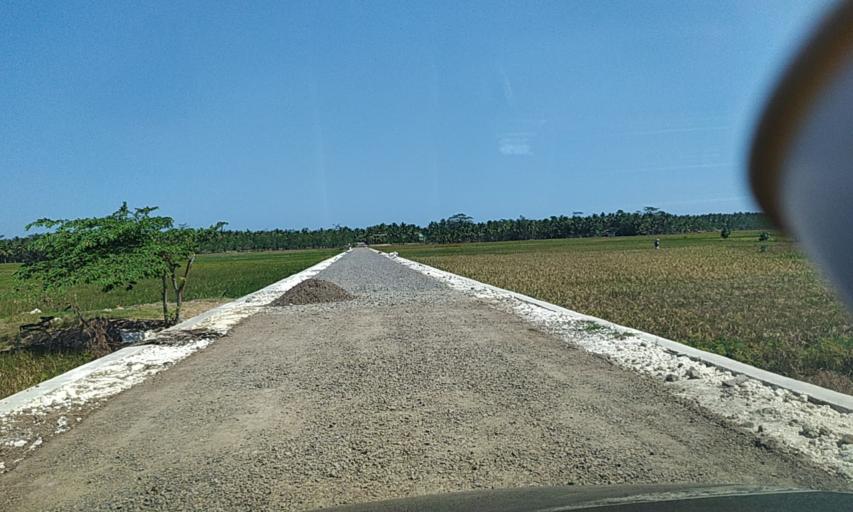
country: ID
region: Central Java
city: Kalenaren
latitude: -7.5964
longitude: 108.7950
